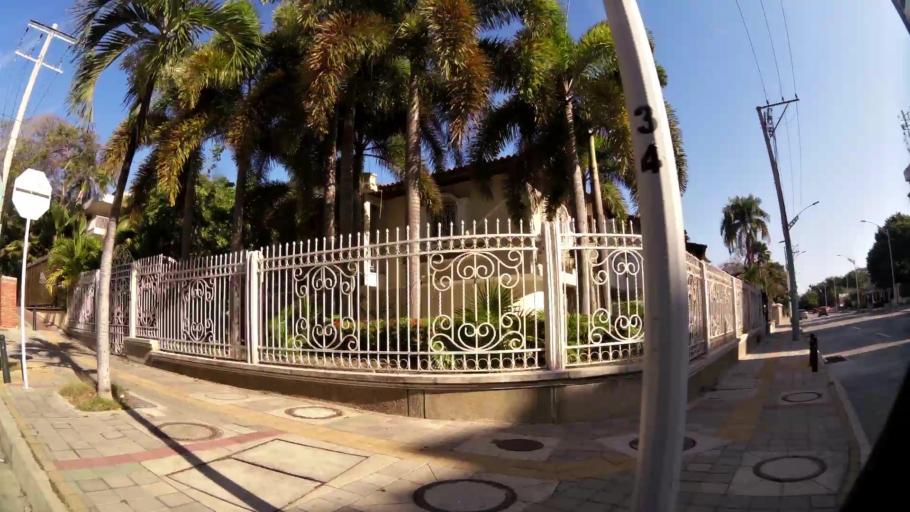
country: CO
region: Atlantico
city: Barranquilla
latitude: 11.0078
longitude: -74.8058
